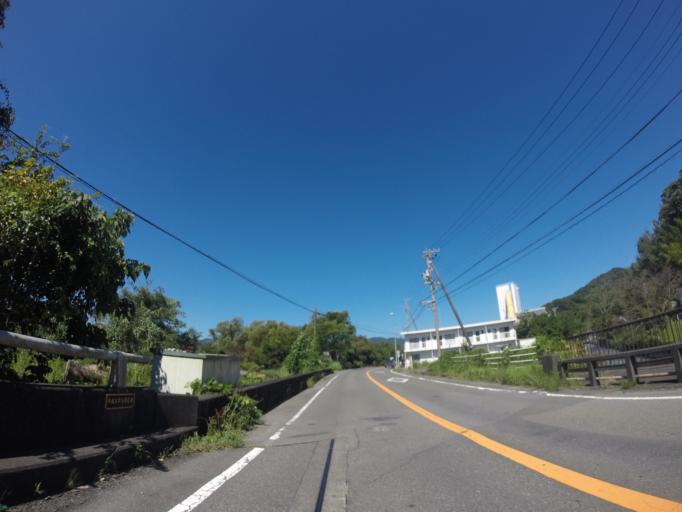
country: JP
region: Shizuoka
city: Kanaya
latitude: 34.8497
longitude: 138.1423
